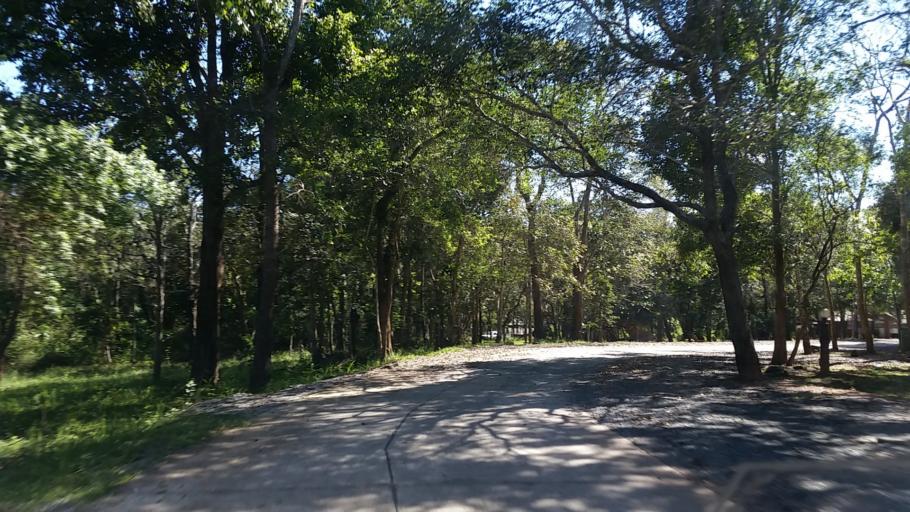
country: TH
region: Chaiyaphum
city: Sap Yai
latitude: 15.6342
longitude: 101.3951
